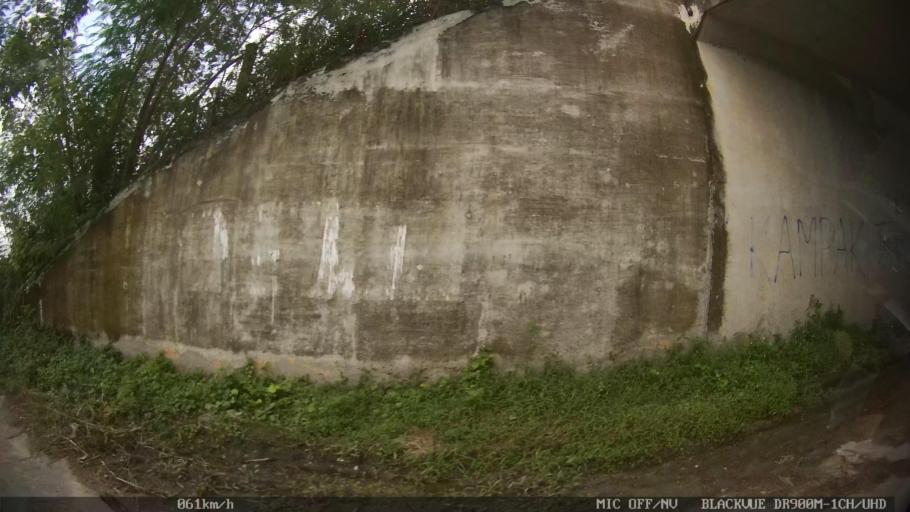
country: ID
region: North Sumatra
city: Percut
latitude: 3.5721
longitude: 98.8468
